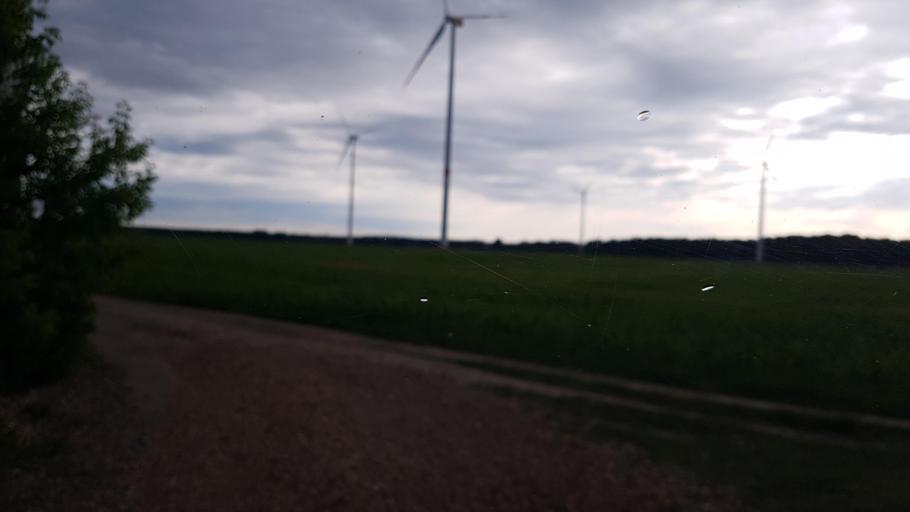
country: DE
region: Brandenburg
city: Bronkow
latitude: 51.6412
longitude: 13.8760
